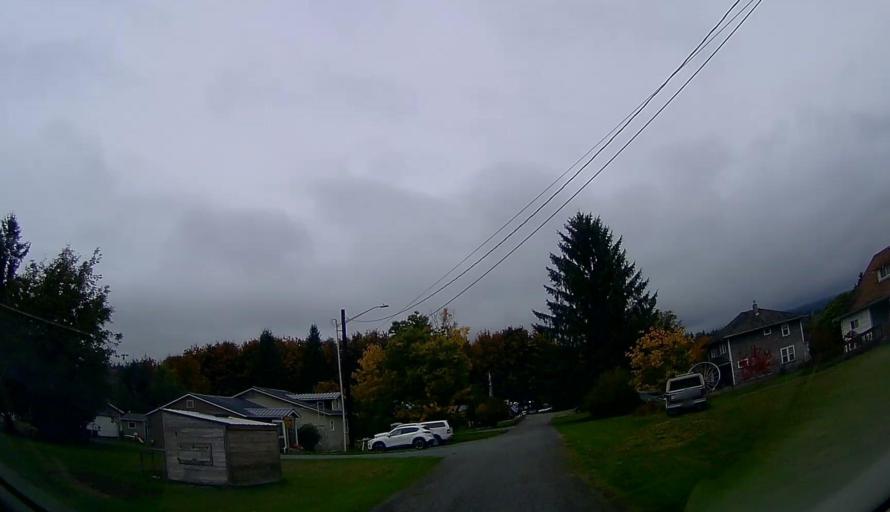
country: US
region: Washington
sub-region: Skagit County
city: Sedro-Woolley
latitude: 48.5249
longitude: -122.0612
